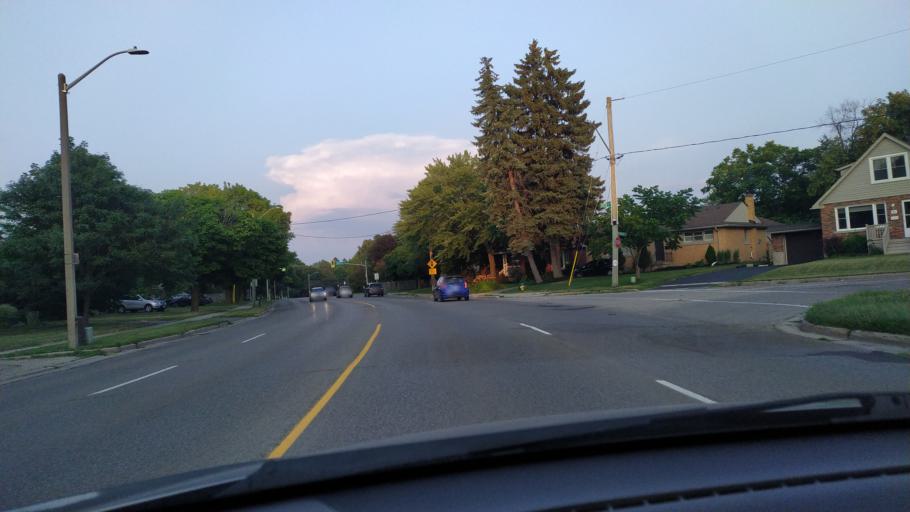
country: CA
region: Ontario
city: Waterloo
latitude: 43.4572
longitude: -80.5341
